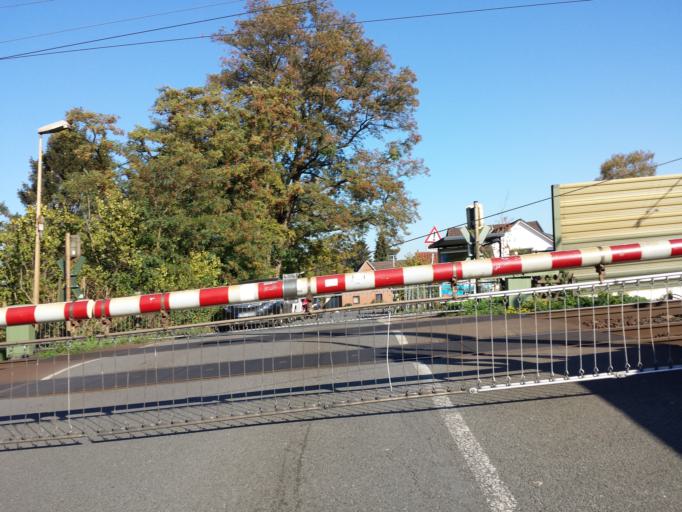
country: DE
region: Lower Saxony
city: Ritterhude
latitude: 53.1458
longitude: 8.7206
